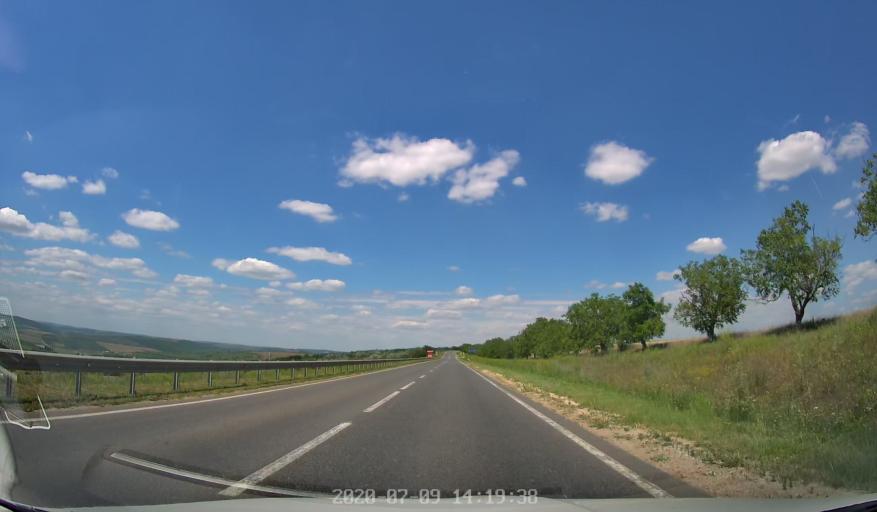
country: MD
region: Rezina
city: Saharna
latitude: 47.6023
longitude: 28.8256
